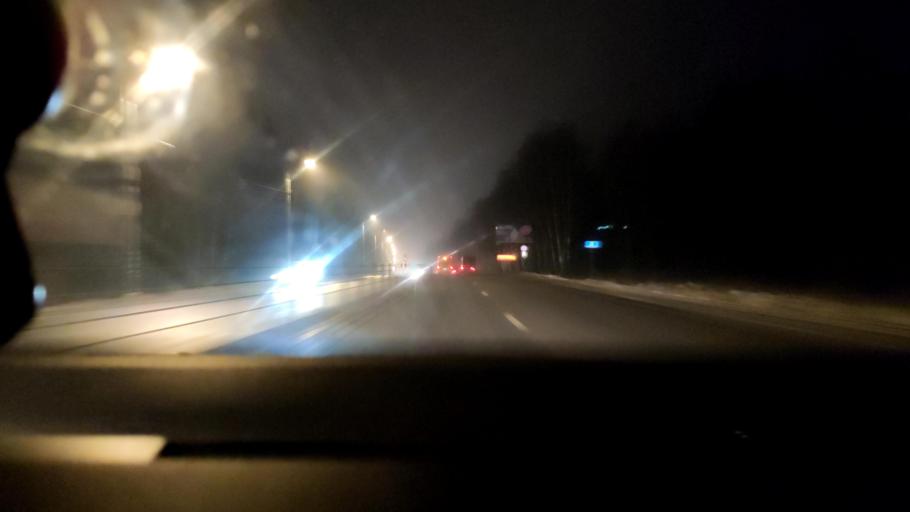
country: RU
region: Moskovskaya
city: Sergiyev Posad
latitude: 56.2393
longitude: 38.1145
